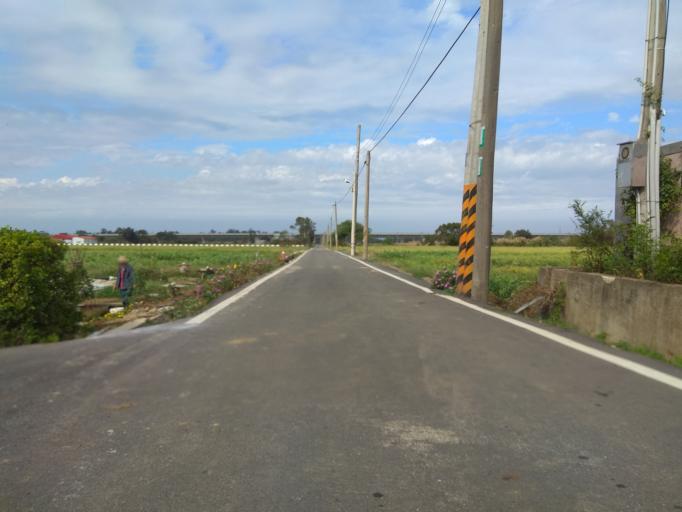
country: TW
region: Taiwan
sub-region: Hsinchu
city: Zhubei
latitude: 24.9535
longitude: 121.0102
